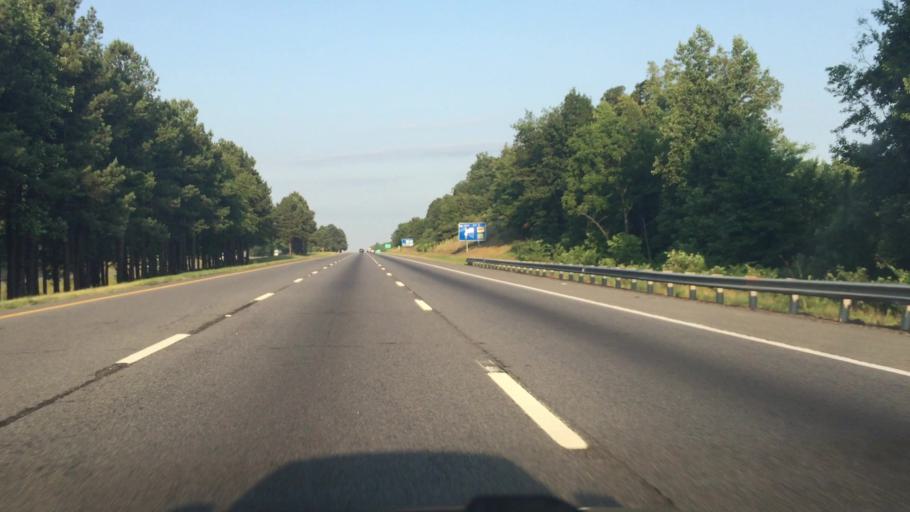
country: US
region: North Carolina
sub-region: Davidson County
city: Lexington
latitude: 35.7852
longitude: -80.2436
